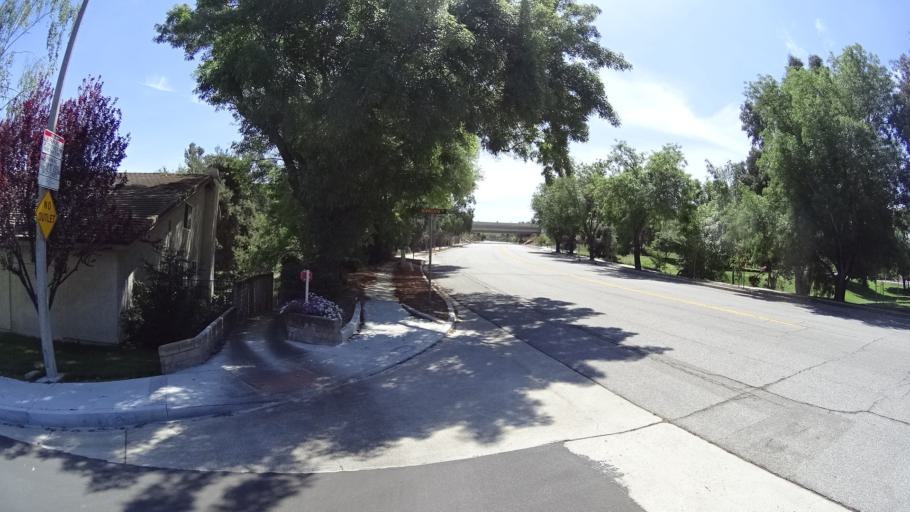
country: US
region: California
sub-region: Ventura County
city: Moorpark
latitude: 34.2368
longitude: -118.8438
